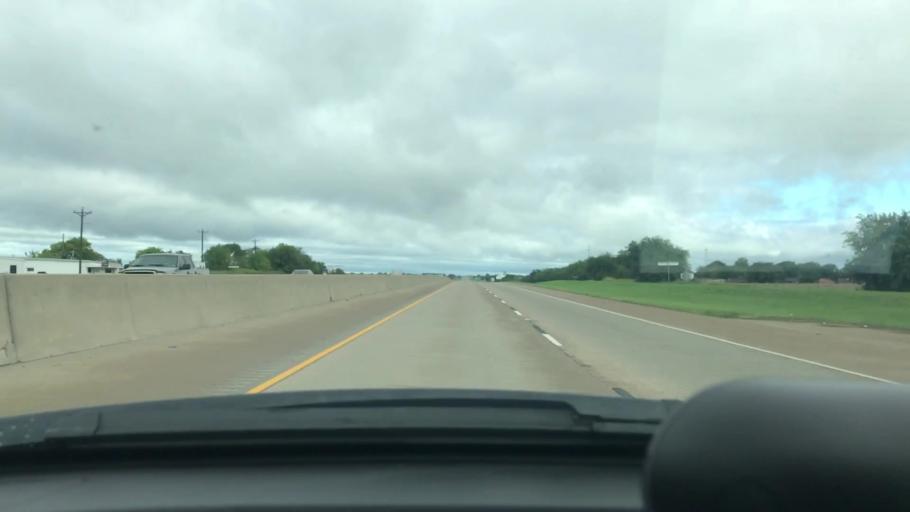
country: US
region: Texas
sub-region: Grayson County
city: Van Alstyne
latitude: 33.4363
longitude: -96.5969
